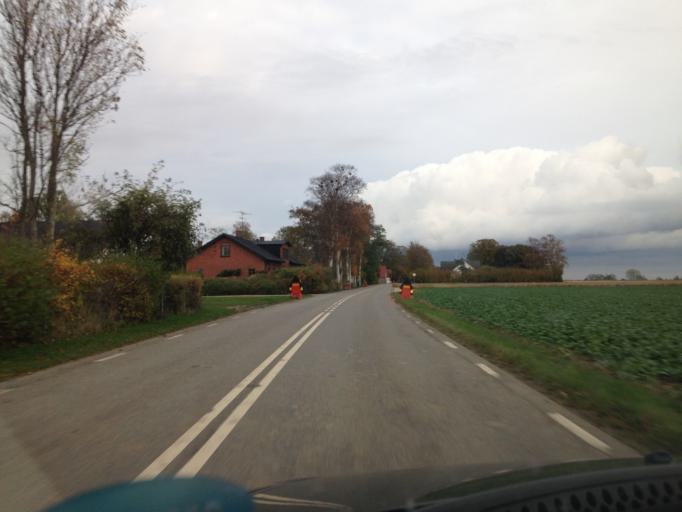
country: SE
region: Skane
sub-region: Ystads Kommun
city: Kopingebro
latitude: 55.4280
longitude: 14.1466
